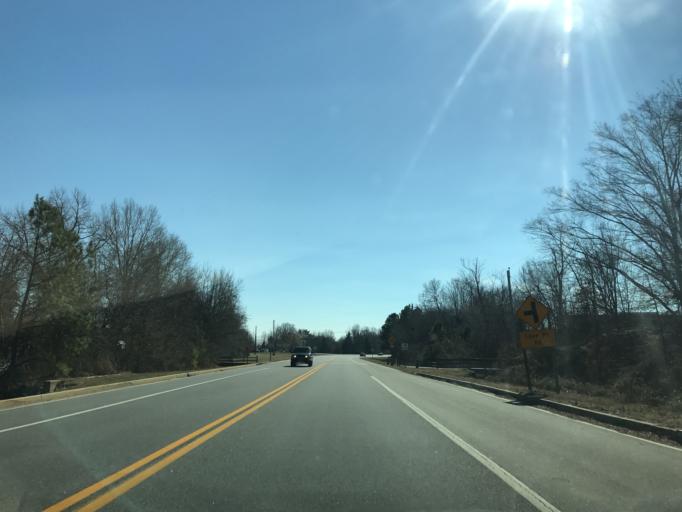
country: US
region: Maryland
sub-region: Queen Anne's County
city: Stevensville
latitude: 38.9904
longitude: -76.3118
